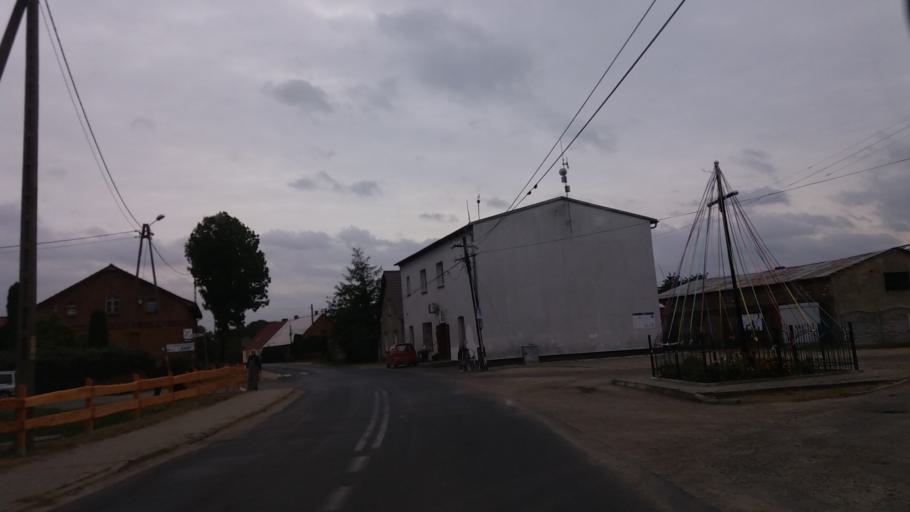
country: PL
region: Lubusz
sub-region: Powiat strzelecko-drezdenecki
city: Strzelce Krajenskie
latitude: 52.9279
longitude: 15.5623
